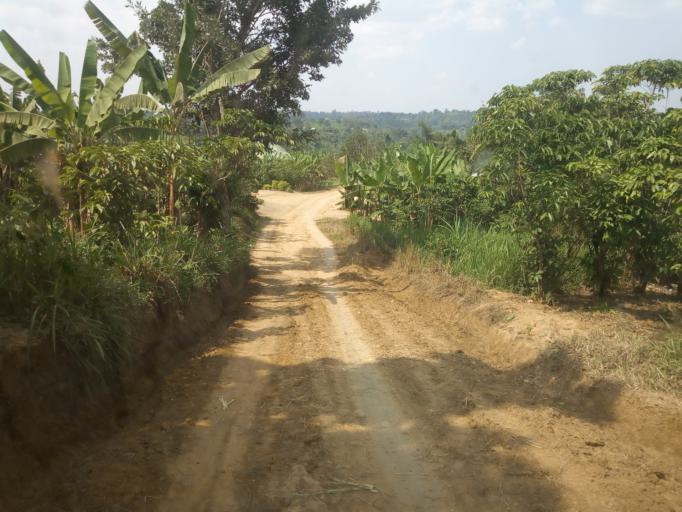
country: UG
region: Western Region
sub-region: Kanungu District
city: Ntungamo
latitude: -0.7891
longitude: 29.6539
